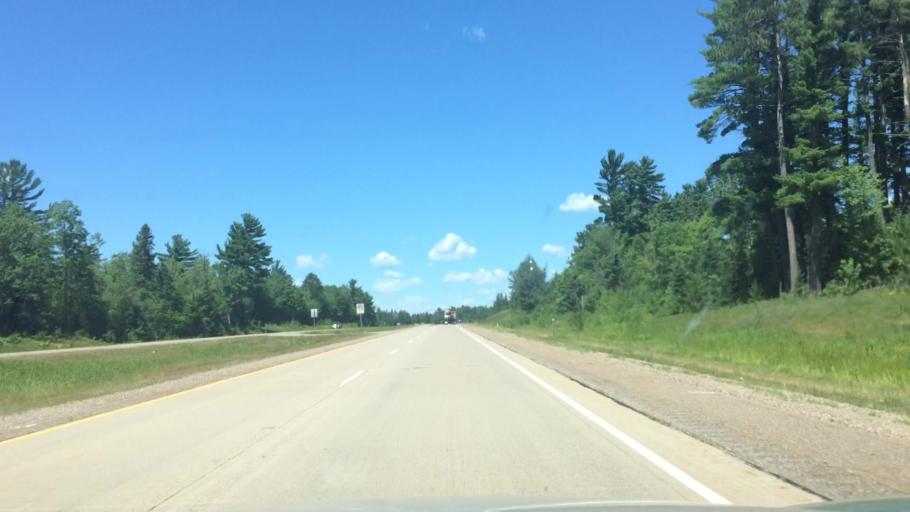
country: US
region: Wisconsin
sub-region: Lincoln County
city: Tomahawk
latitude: 45.4393
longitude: -89.6824
